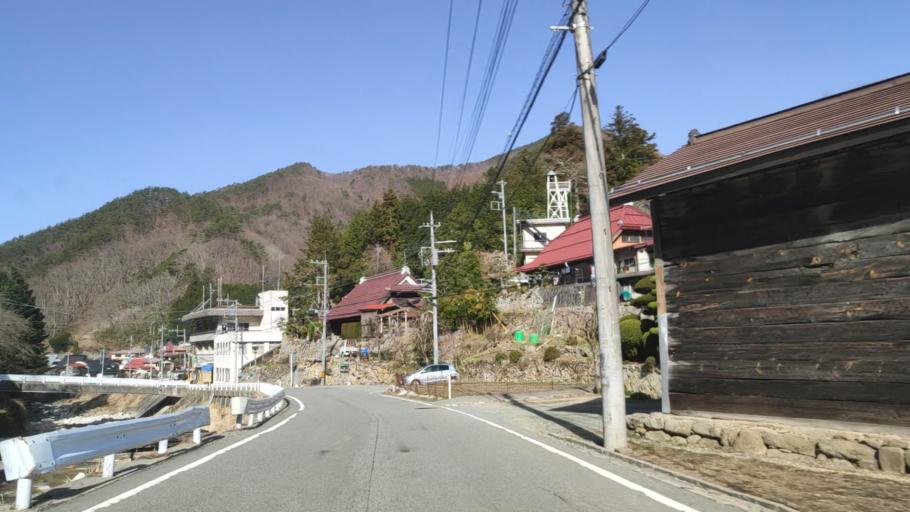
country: JP
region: Yamanashi
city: Fujikawaguchiko
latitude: 35.5532
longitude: 138.6666
